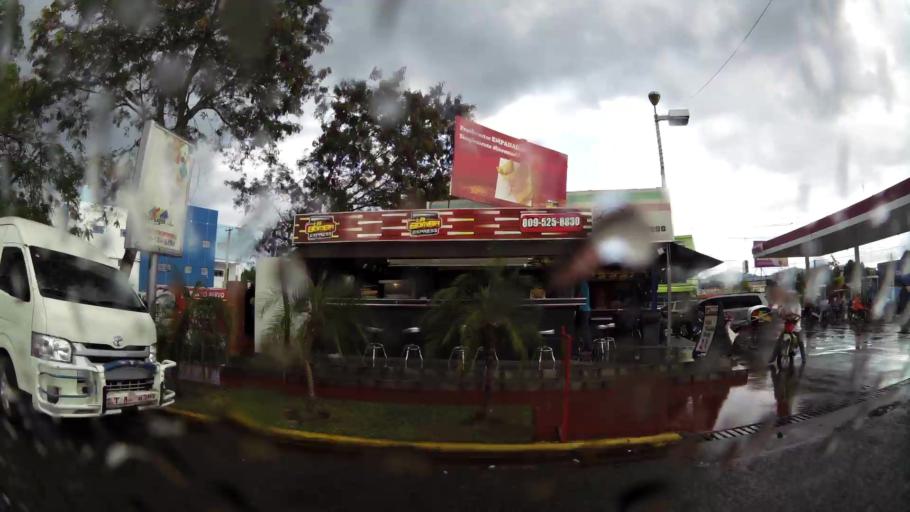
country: DO
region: Monsenor Nouel
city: Bonao
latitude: 18.9370
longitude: -70.4110
